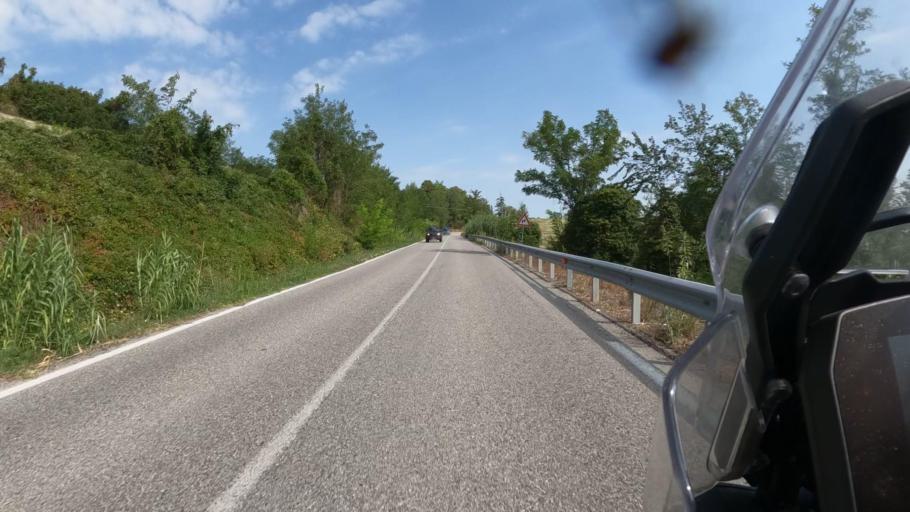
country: IT
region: Piedmont
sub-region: Provincia di Alessandria
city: Rosignano Monferrato
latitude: 45.0859
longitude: 8.4132
